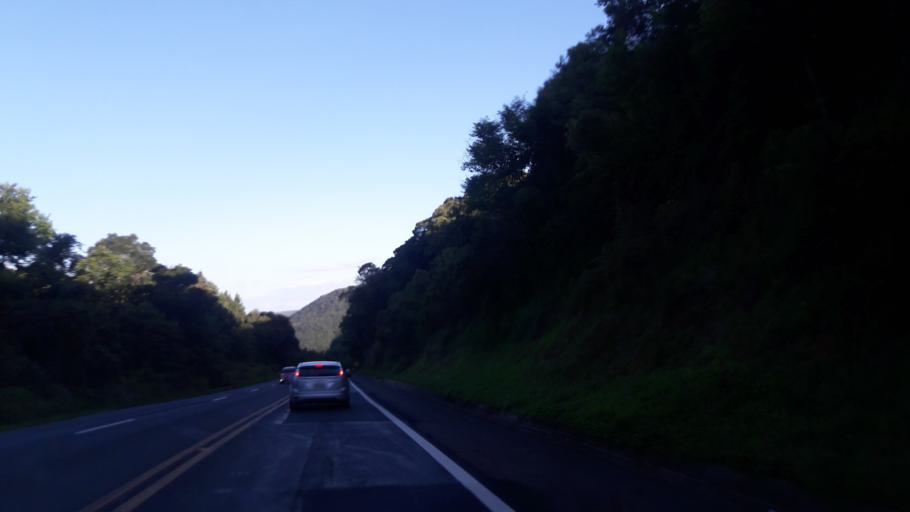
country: BR
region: Parana
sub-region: Prudentopolis
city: Prudentopolis
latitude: -25.3115
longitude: -51.2055
